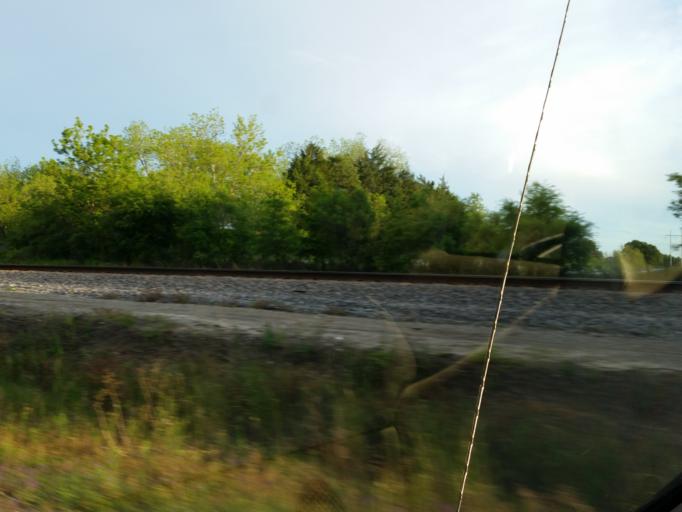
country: US
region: Georgia
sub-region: Tift County
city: Tifton
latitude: 31.5507
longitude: -83.5545
